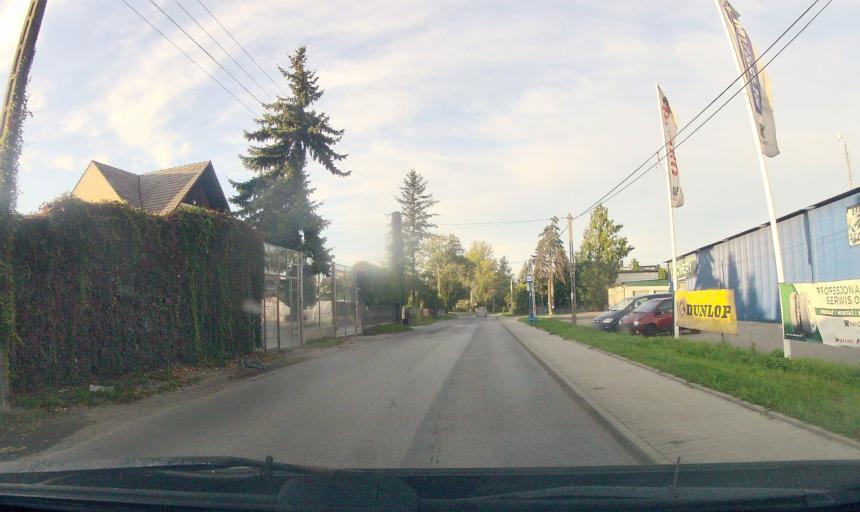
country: PL
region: Lesser Poland Voivodeship
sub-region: Powiat wielicki
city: Kokotow
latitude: 50.0552
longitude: 20.0495
